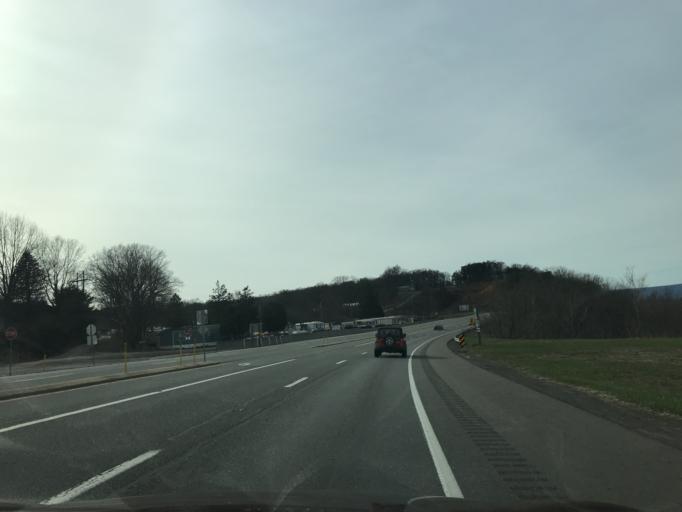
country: US
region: Pennsylvania
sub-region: Northumberland County
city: Dewart
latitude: 41.0913
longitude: -76.8828
